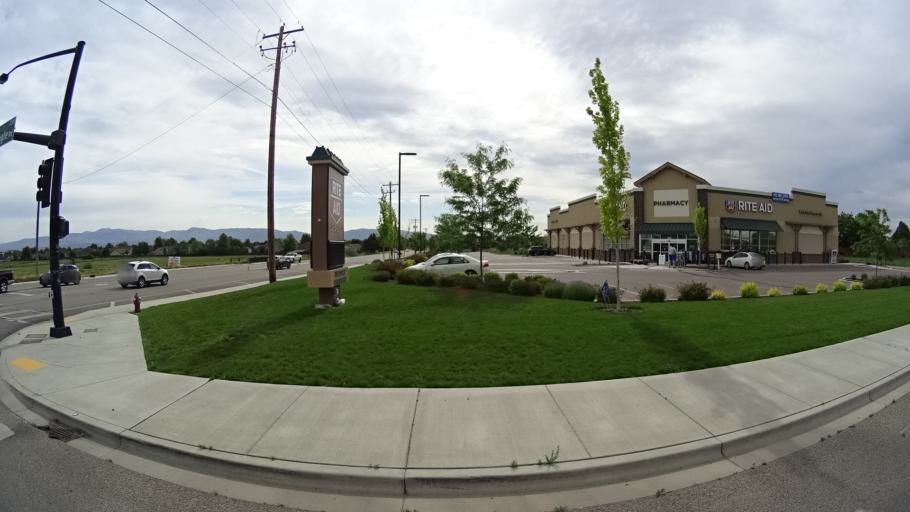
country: US
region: Idaho
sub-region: Ada County
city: Meridian
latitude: 43.5755
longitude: -116.3544
